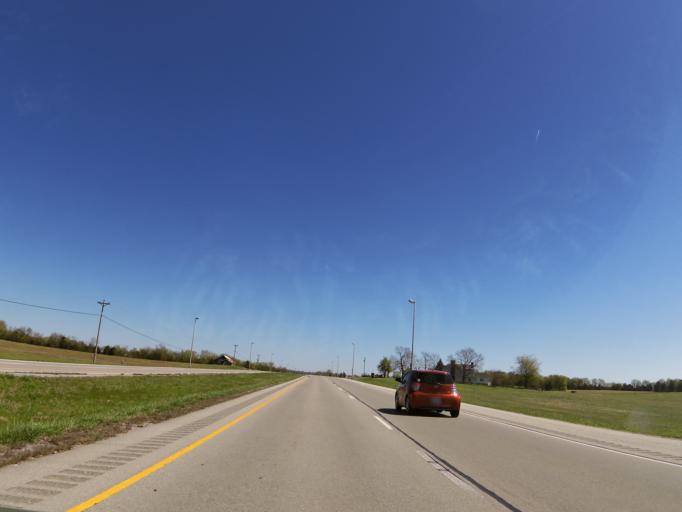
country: US
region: Kentucky
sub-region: Warren County
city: Bowling Green
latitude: 36.9401
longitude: -86.5310
